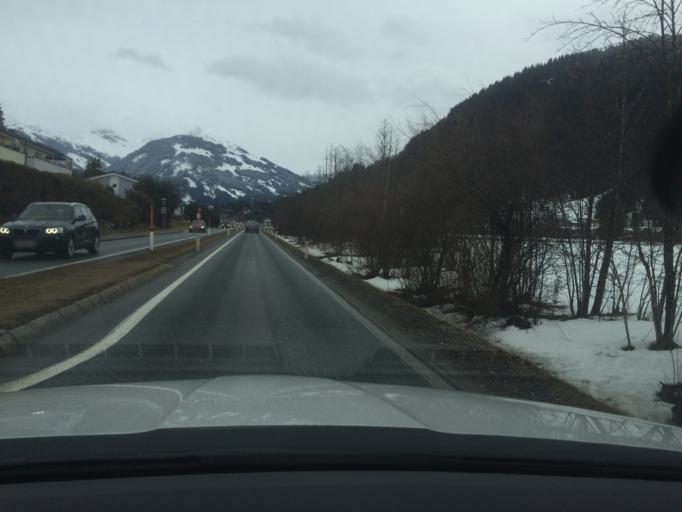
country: AT
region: Tyrol
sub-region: Politischer Bezirk Kitzbuhel
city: Kitzbuhel
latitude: 47.4308
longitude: 12.4087
